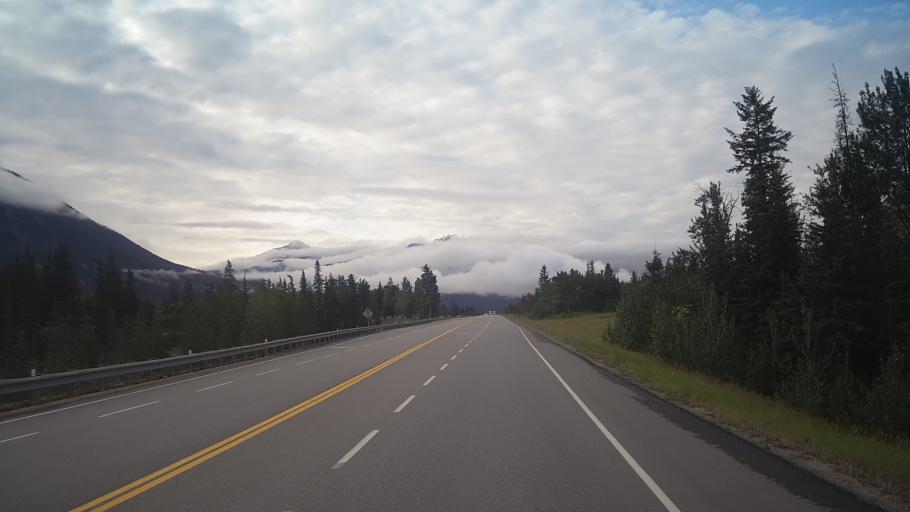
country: CA
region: Alberta
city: Jasper Park Lodge
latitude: 52.9641
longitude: -118.0522
